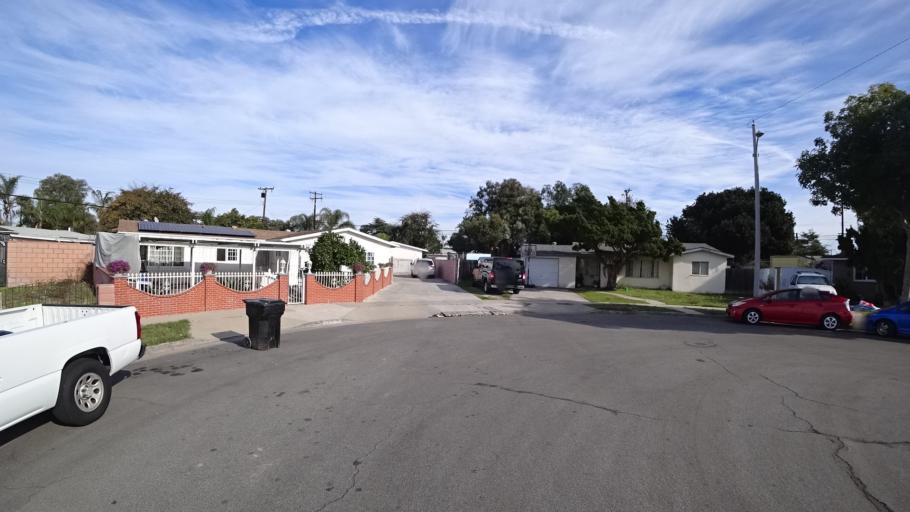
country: US
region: California
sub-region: Orange County
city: Garden Grove
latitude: 33.7618
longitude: -117.9078
